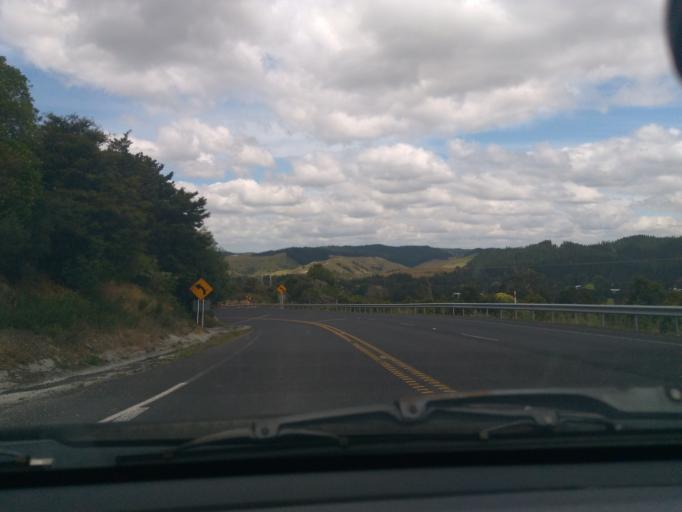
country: NZ
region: Northland
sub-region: Far North District
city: Moerewa
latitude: -35.3899
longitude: 173.9978
